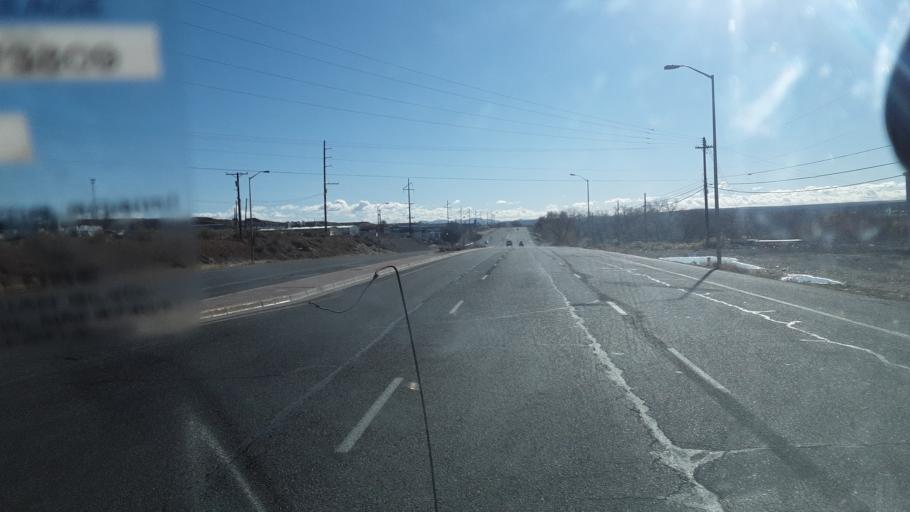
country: US
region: New Mexico
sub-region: San Juan County
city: Farmington
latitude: 36.7172
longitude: -108.1542
